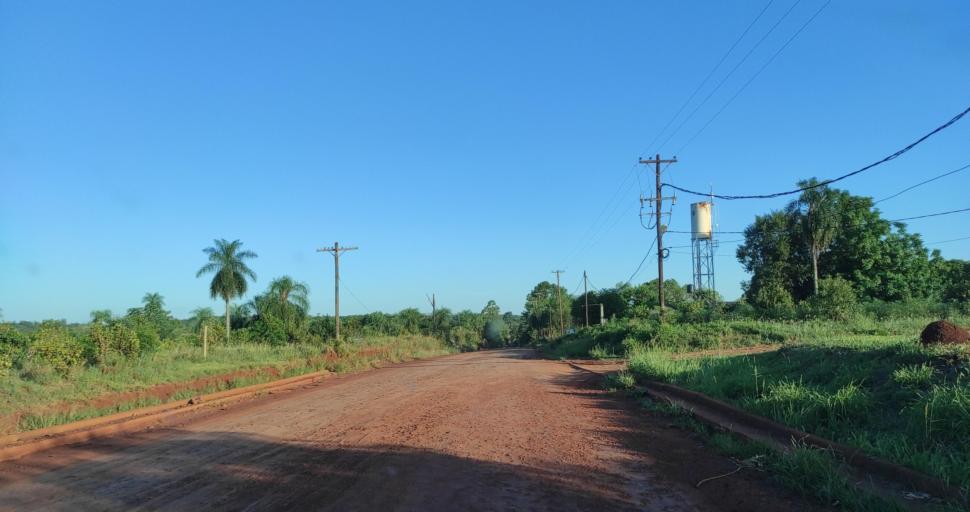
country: AR
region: Misiones
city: Gobernador Roca
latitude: -27.1964
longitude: -55.4657
